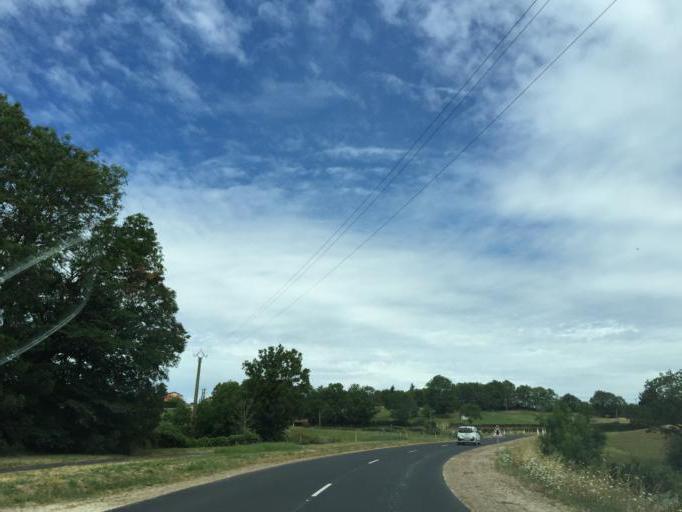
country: FR
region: Rhone-Alpes
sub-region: Departement de la Loire
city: Saint-Bonnet-le-Chateau
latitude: 45.4162
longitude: 4.0855
